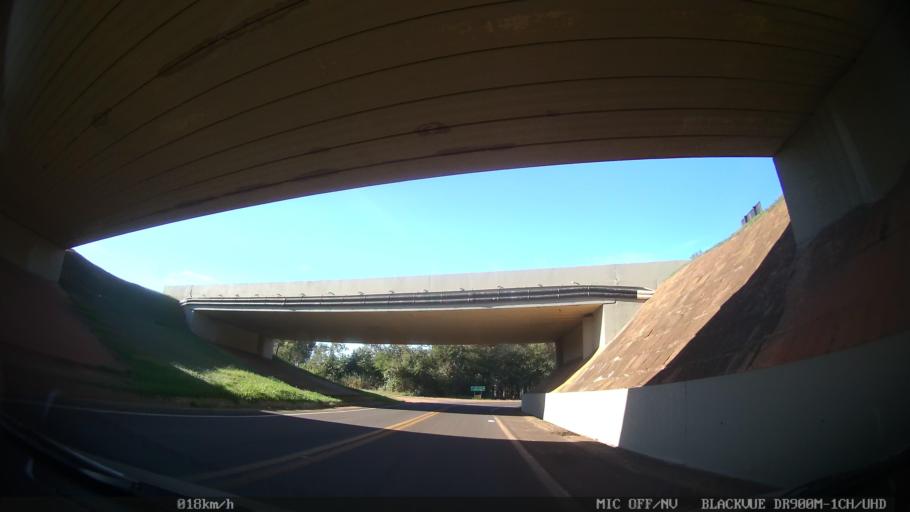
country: BR
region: Sao Paulo
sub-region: Sao Jose Do Rio Preto
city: Sao Jose do Rio Preto
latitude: -20.8837
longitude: -49.3144
